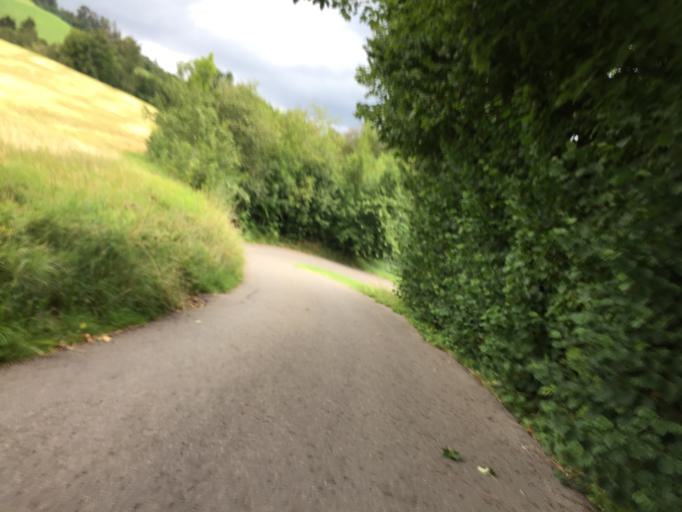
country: CH
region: Bern
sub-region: Bern-Mittelland District
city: Munsingen
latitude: 46.8637
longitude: 7.5447
